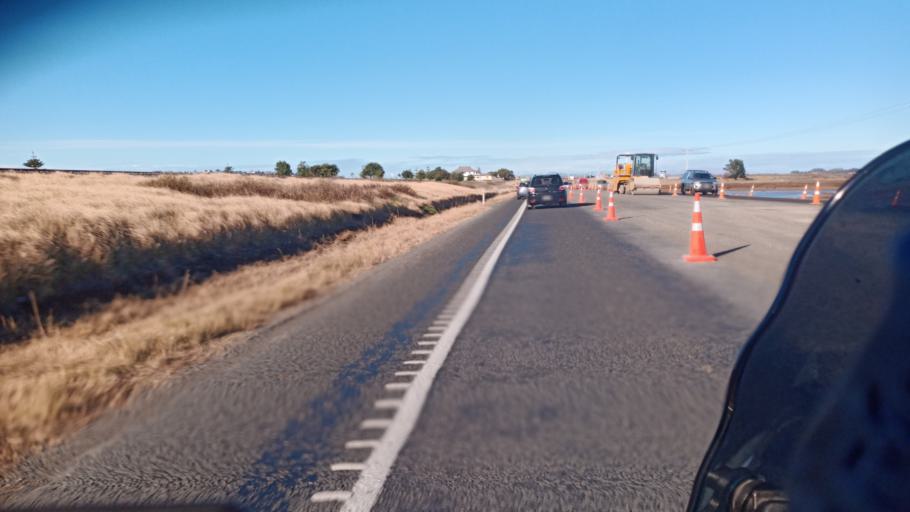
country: NZ
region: Hawke's Bay
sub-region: Napier City
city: Napier
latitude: -39.4549
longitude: 176.8718
